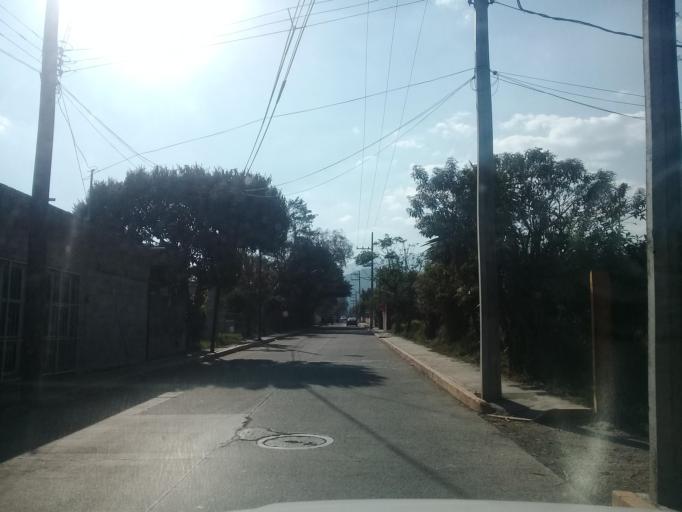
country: MX
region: Veracruz
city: Jalapilla
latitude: 18.8428
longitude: -97.0798
